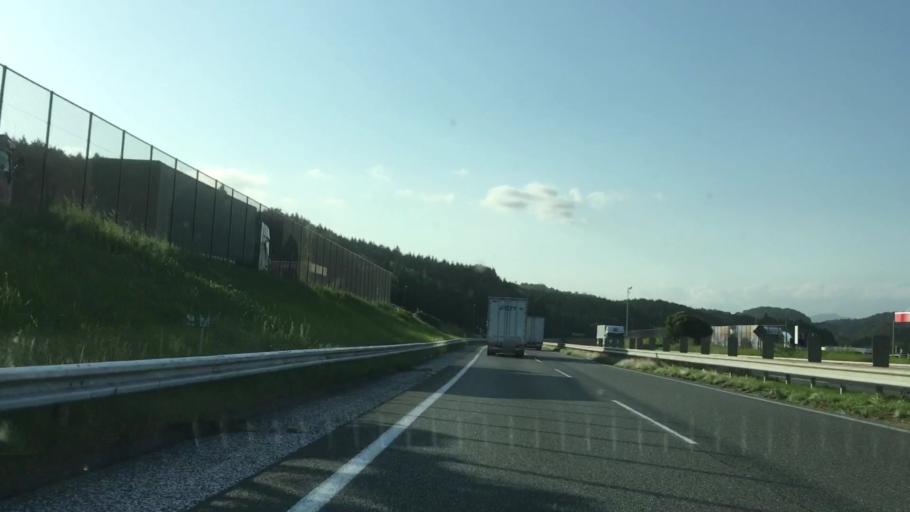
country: JP
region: Yamaguchi
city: Ogori-shimogo
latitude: 34.1532
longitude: 131.3382
